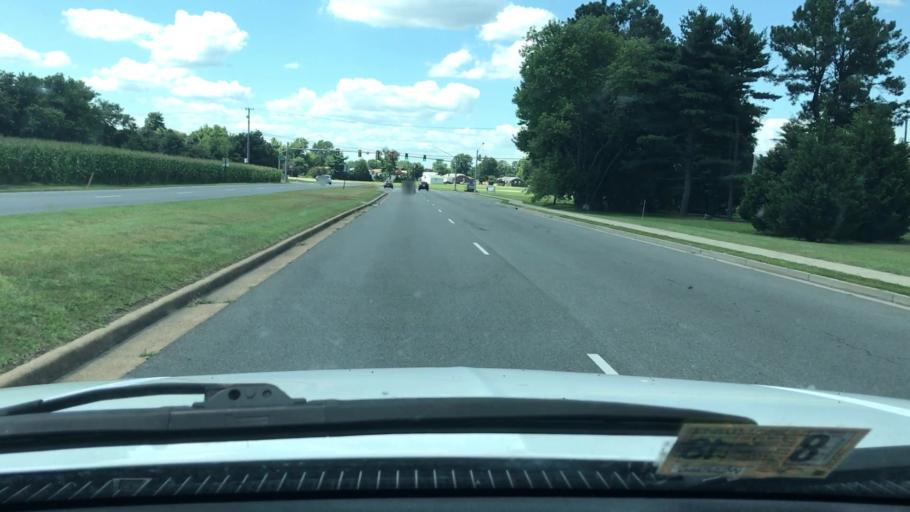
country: US
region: Virginia
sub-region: Henrico County
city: East Highland Park
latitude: 37.5706
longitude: -77.3812
